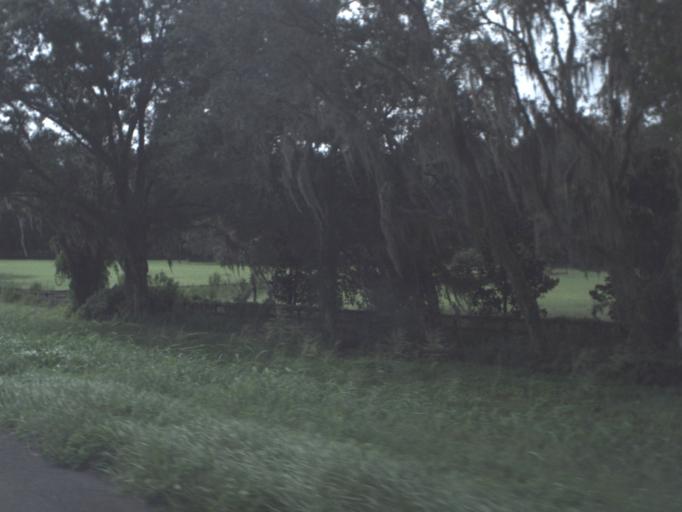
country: US
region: Florida
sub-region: Pasco County
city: Zephyrhills North
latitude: 28.2878
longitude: -82.1269
